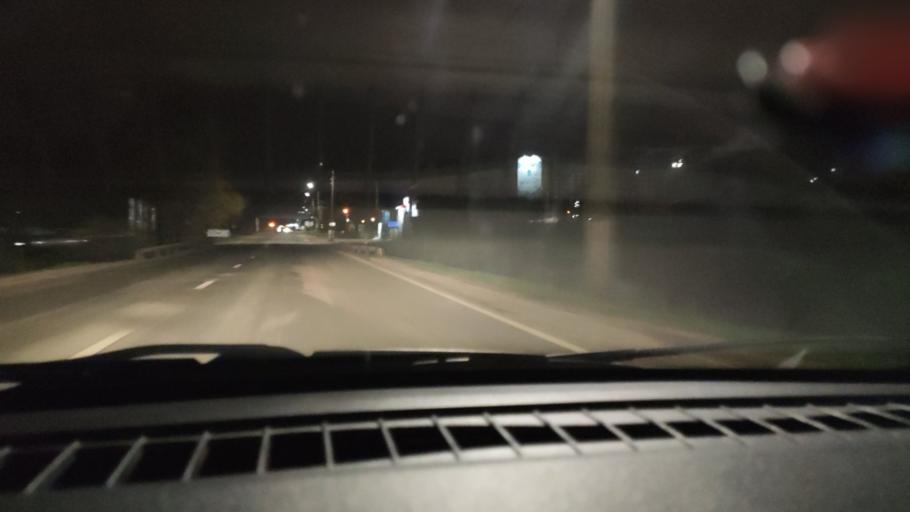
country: RU
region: Bashkortostan
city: Sterlitamak
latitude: 53.6430
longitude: 55.8946
